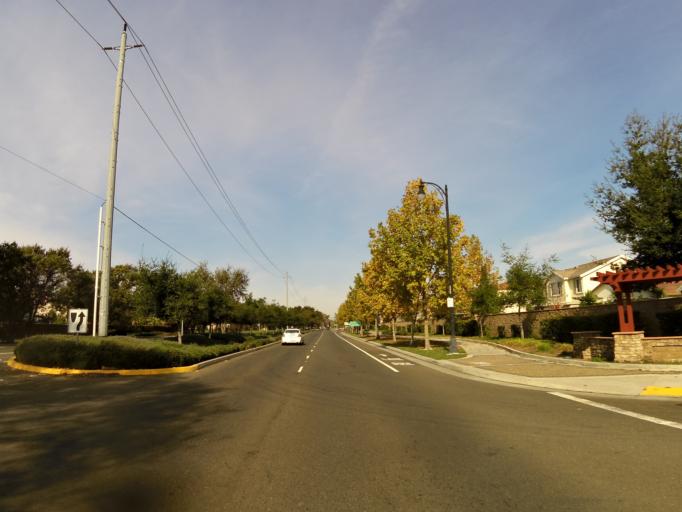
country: US
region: California
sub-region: Sacramento County
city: Laguna
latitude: 38.4026
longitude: -121.4175
